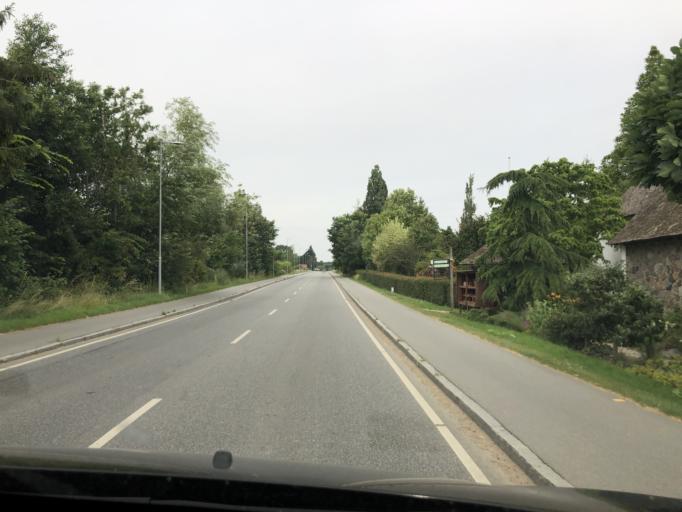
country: DK
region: South Denmark
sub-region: Assens Kommune
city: Glamsbjerg
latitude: 55.2572
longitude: 10.1324
